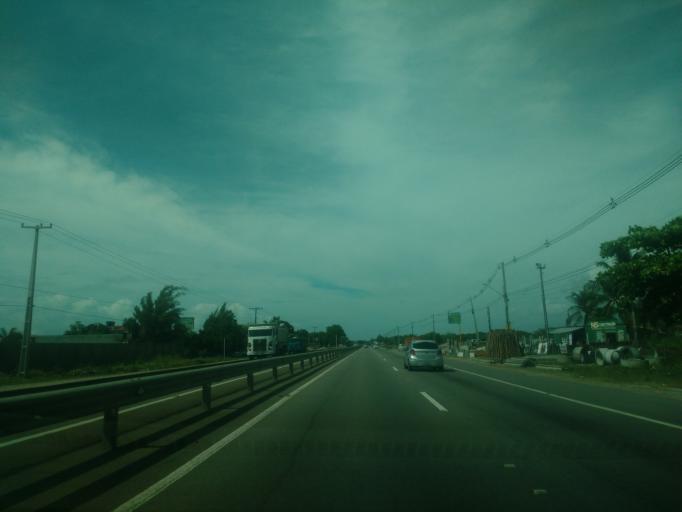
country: BR
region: Alagoas
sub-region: Marechal Deodoro
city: Marechal Deodoro
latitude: -9.7494
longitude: -35.8395
